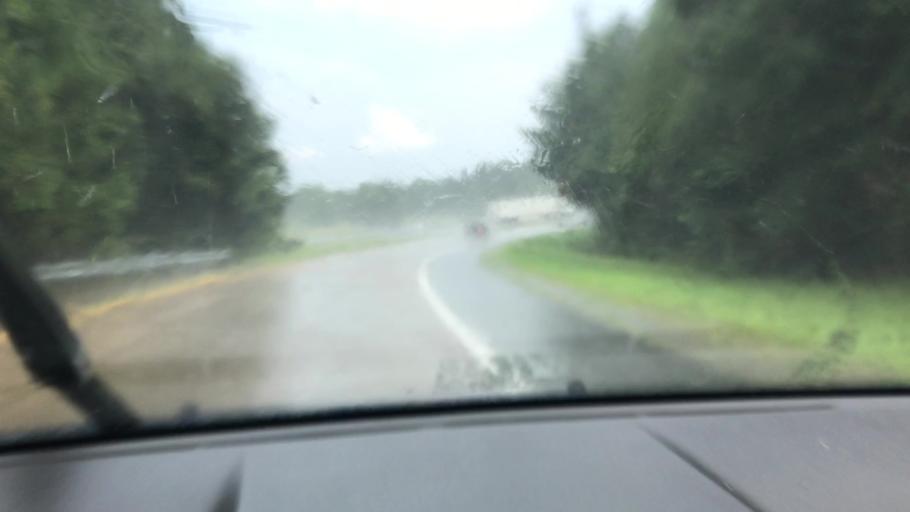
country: US
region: Virginia
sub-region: Henrico County
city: Chamberlayne
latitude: 37.6567
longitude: -77.4518
